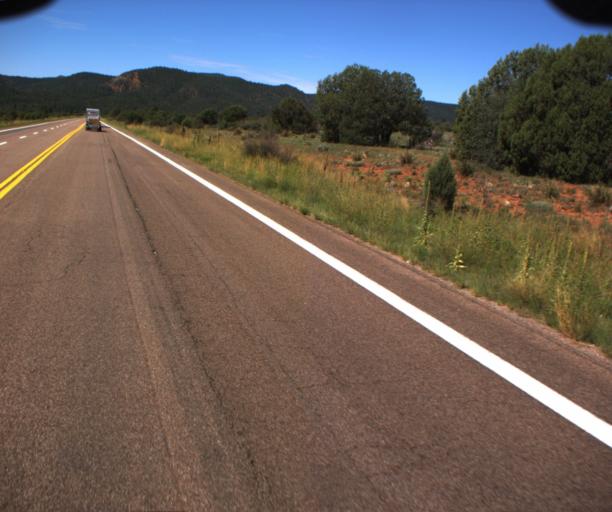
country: US
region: Arizona
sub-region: Navajo County
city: Cibecue
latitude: 33.9647
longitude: -110.3228
